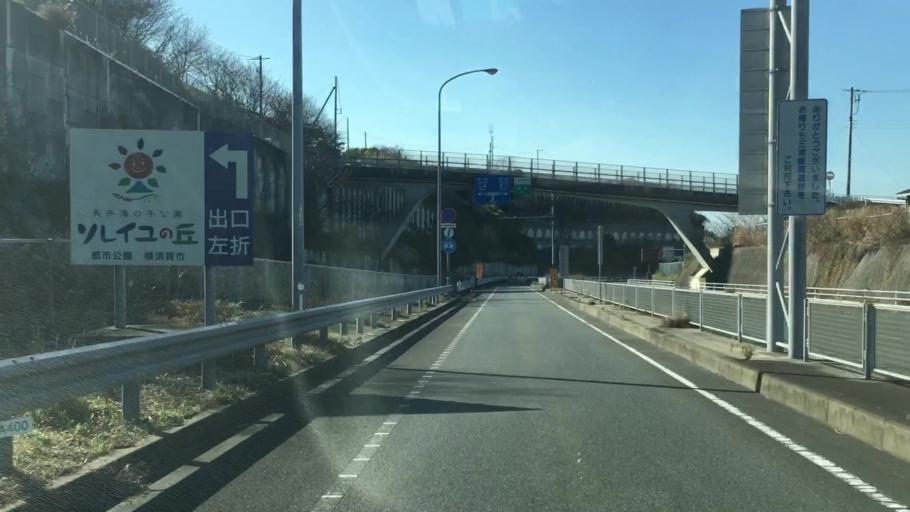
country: JP
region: Kanagawa
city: Miura
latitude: 35.2116
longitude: 139.6358
